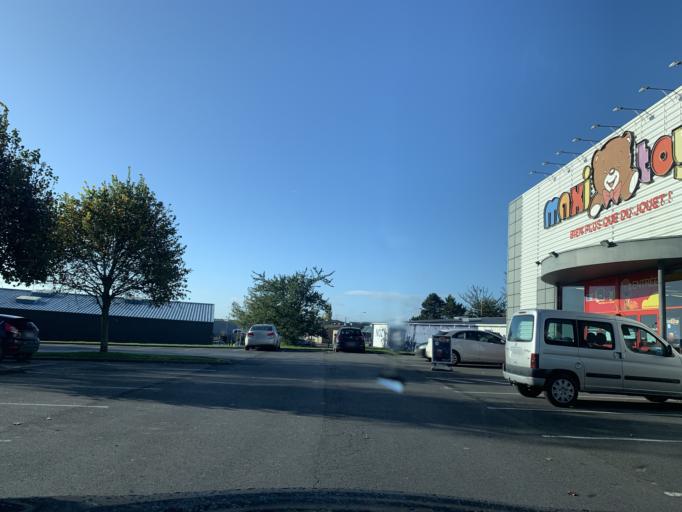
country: FR
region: Nord-Pas-de-Calais
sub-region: Departement du Nord
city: Proville
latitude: 50.1525
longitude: 3.2201
